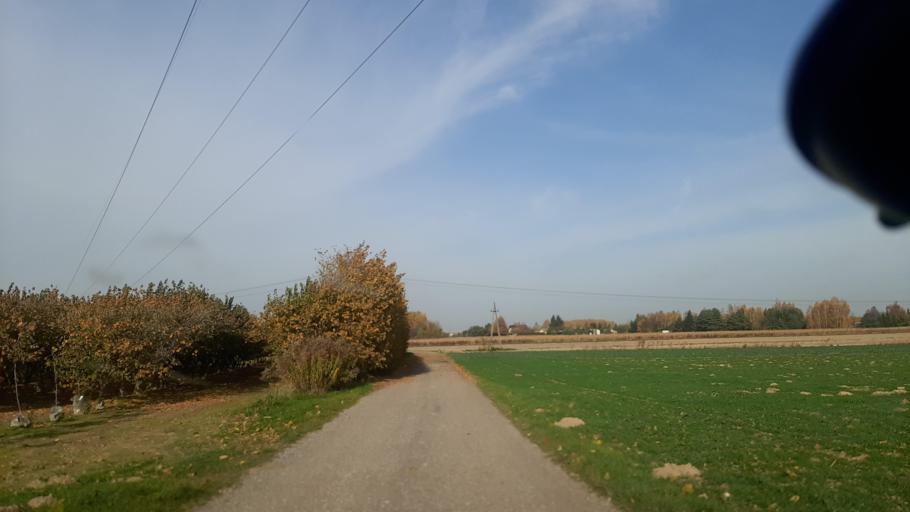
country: PL
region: Lublin Voivodeship
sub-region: Powiat lubelski
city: Lublin
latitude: 51.3303
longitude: 22.5440
